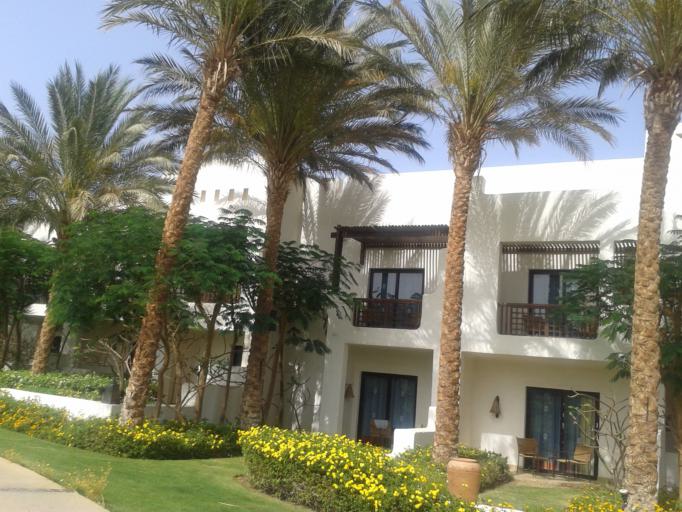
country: EG
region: Red Sea
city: Marsa Alam
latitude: 25.5390
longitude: 34.6399
